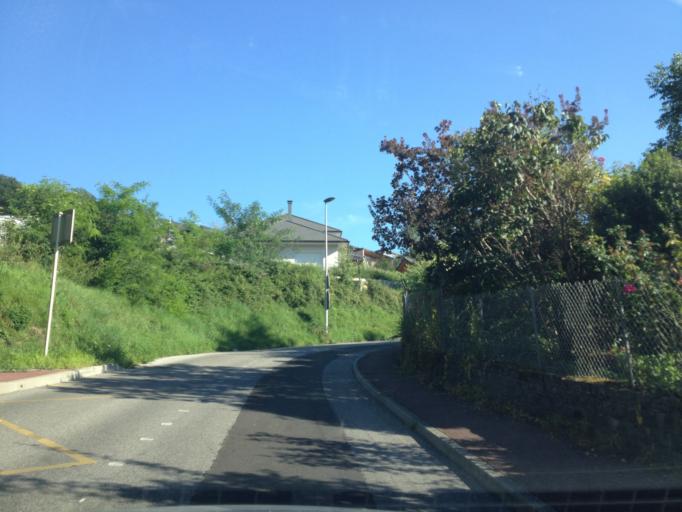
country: FR
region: Rhone-Alpes
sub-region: Departement de la Savoie
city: Voglans
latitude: 45.6296
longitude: 5.8993
